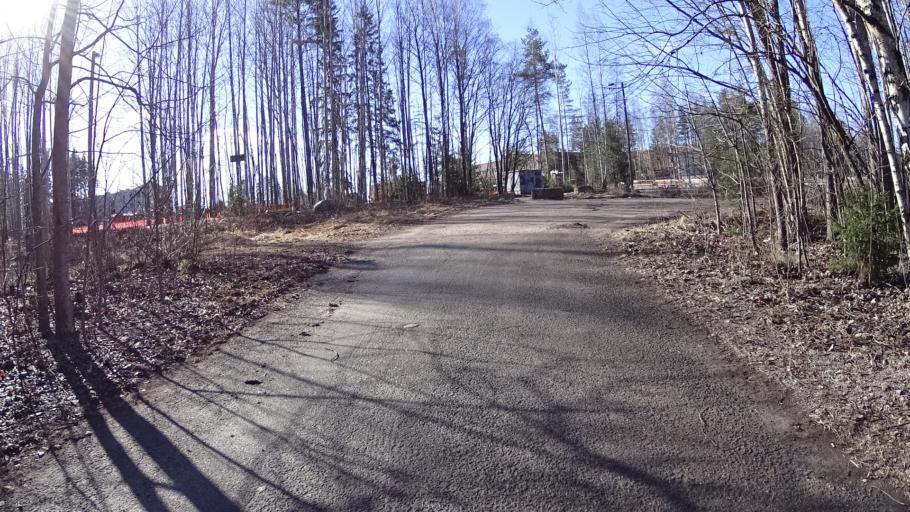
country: FI
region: Uusimaa
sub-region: Helsinki
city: Teekkarikylae
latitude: 60.2640
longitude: 24.8857
